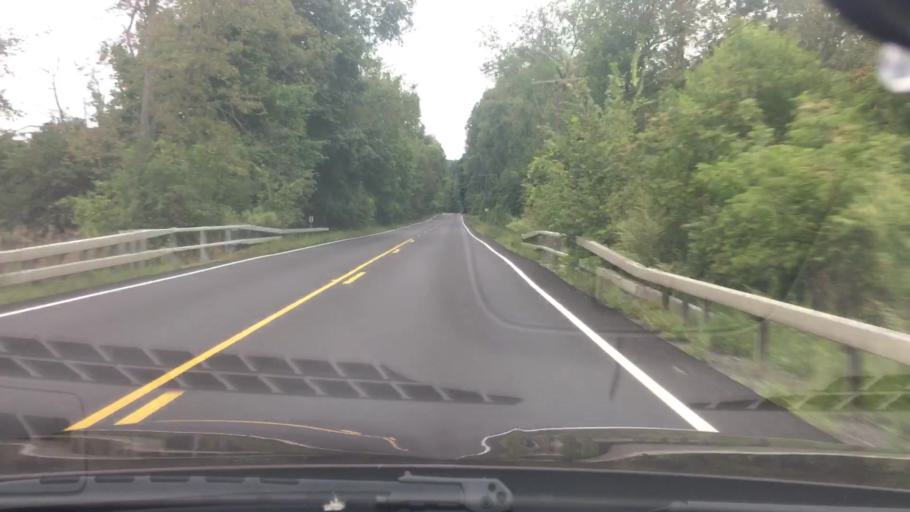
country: US
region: New York
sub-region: Dutchess County
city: Dover Plains
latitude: 41.8646
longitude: -73.5054
